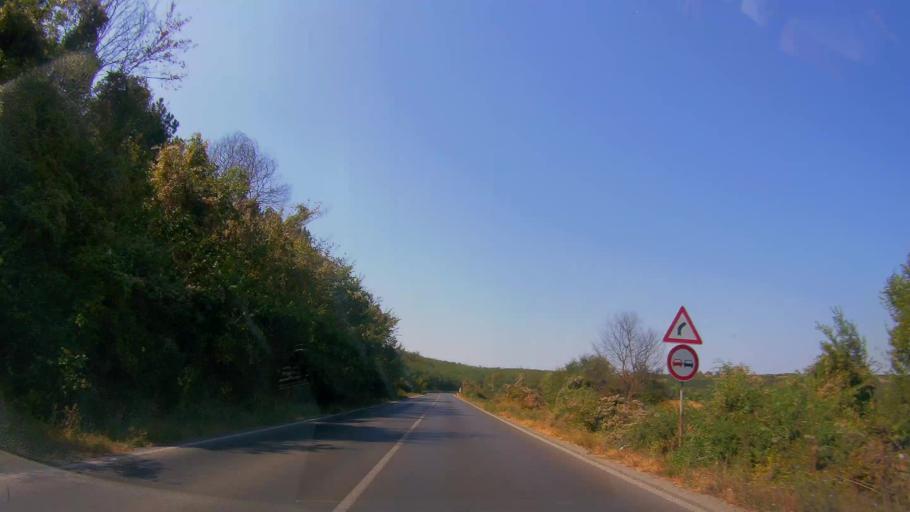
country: BG
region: Razgrad
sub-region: Obshtina Tsar Kaloyan
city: Tsar Kaloyan
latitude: 43.6145
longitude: 26.2182
